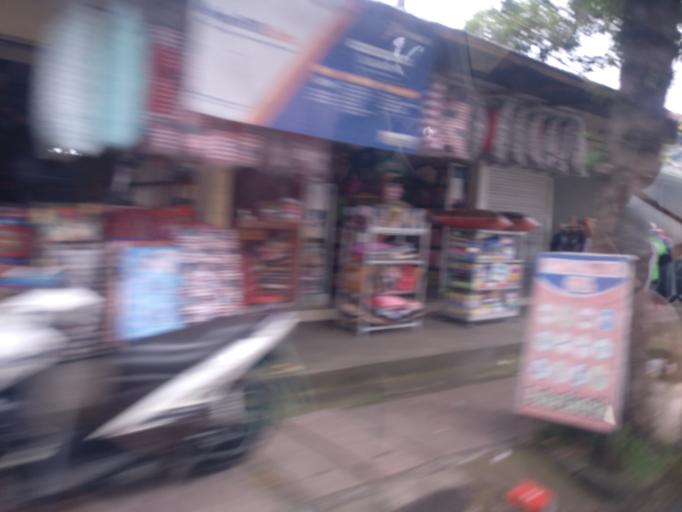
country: ID
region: Bali
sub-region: Kabupaten Gianyar
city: Ubud
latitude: -8.5505
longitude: 115.3031
